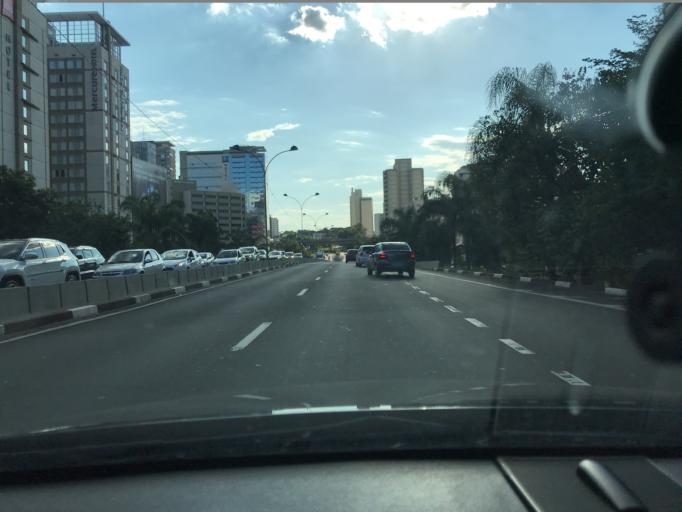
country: BR
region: Sao Paulo
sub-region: Campinas
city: Campinas
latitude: -22.9103
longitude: -47.0551
